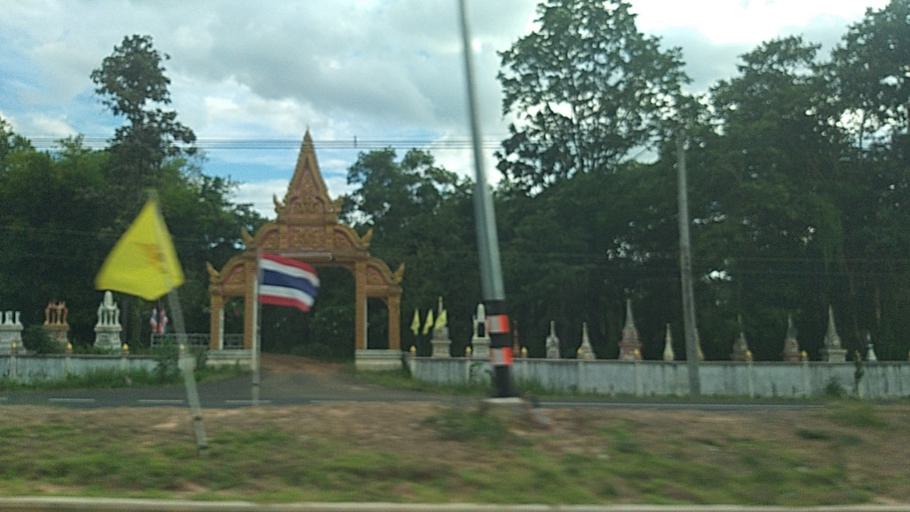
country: TH
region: Surin
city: Kap Choeng
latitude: 14.5572
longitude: 103.5026
